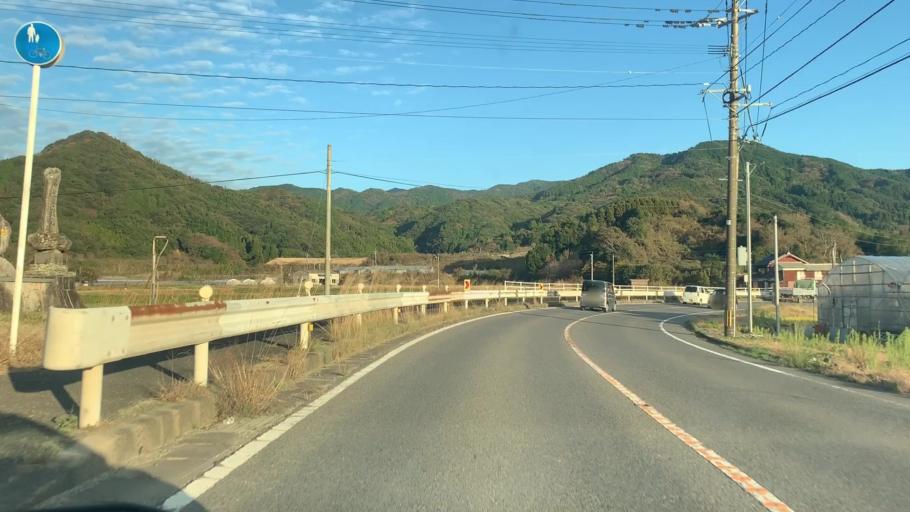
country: JP
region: Saga Prefecture
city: Karatsu
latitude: 33.3805
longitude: 129.9981
